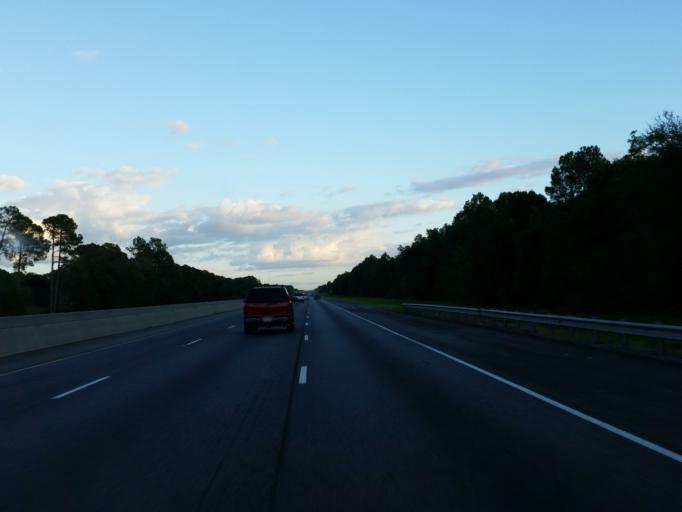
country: US
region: Georgia
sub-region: Turner County
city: Ashburn
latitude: 31.7772
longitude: -83.6835
